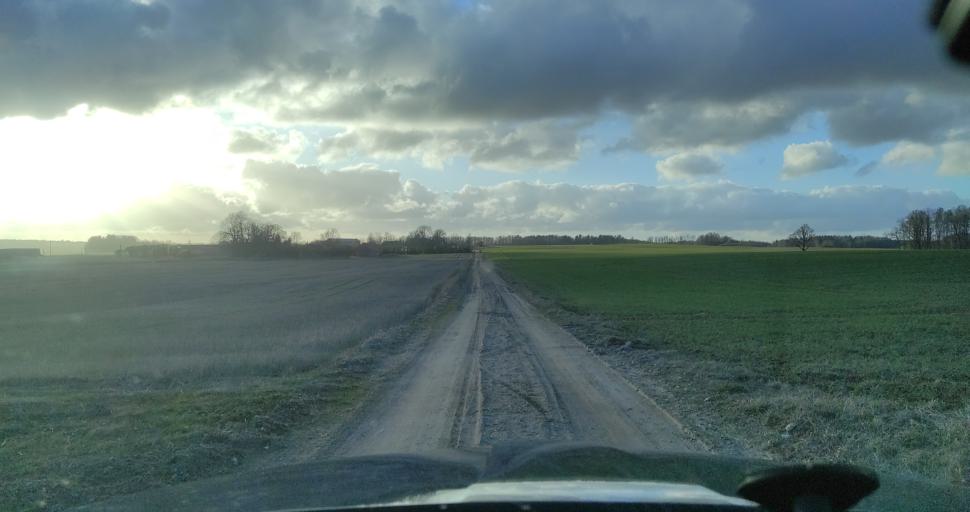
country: LV
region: Aizpute
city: Aizpute
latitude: 56.8473
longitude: 21.7705
